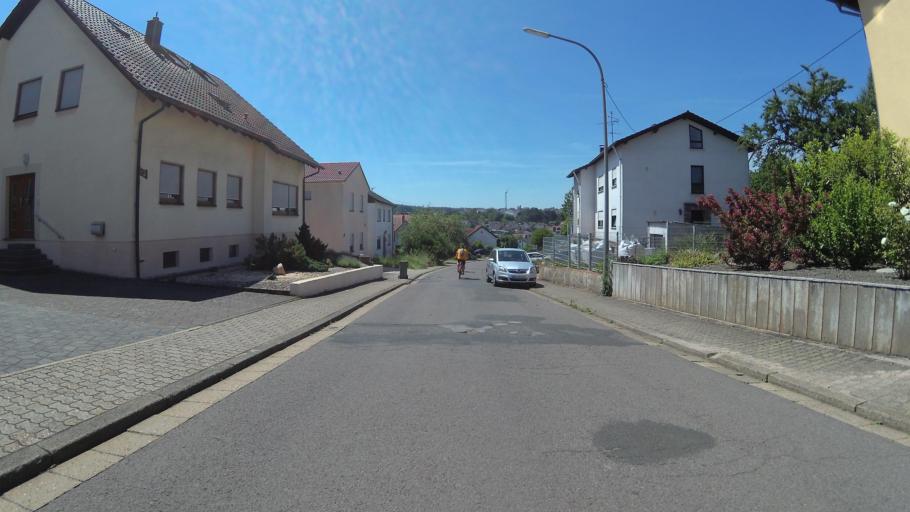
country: DE
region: Saarland
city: Lebach
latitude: 49.3921
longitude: 6.9303
